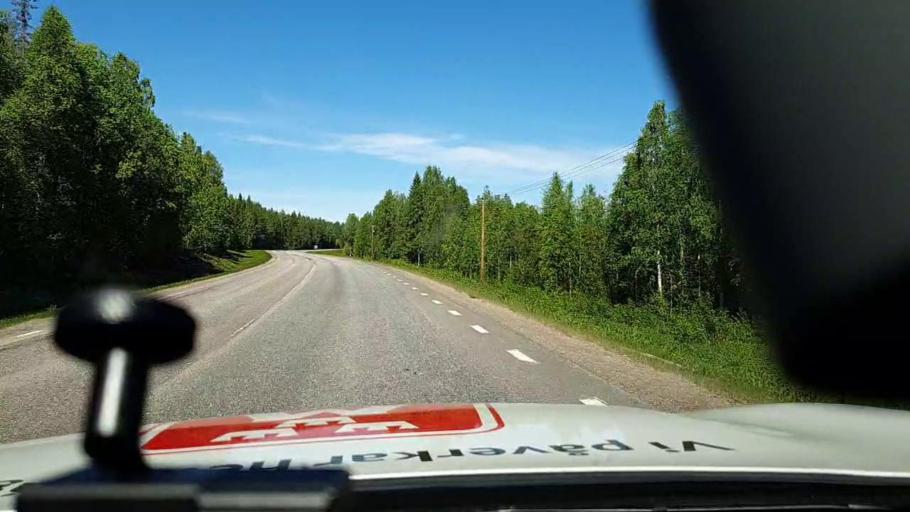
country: SE
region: Norrbotten
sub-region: Kalix Kommun
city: Toere
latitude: 66.1042
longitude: 22.7118
